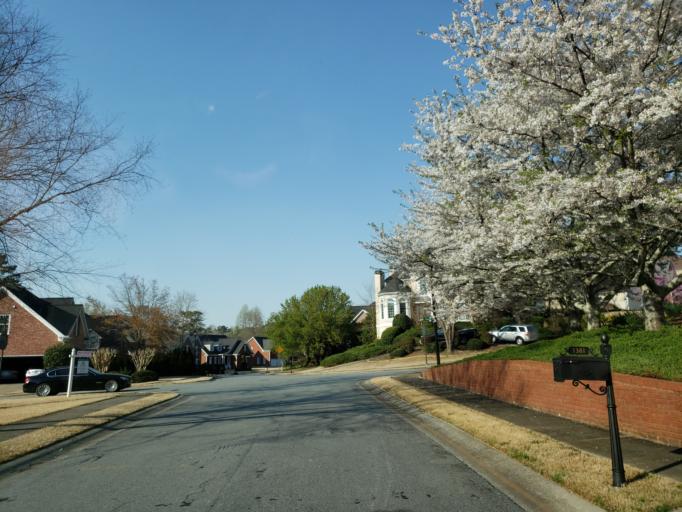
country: US
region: Georgia
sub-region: Cobb County
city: Marietta
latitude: 33.9812
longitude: -84.5126
